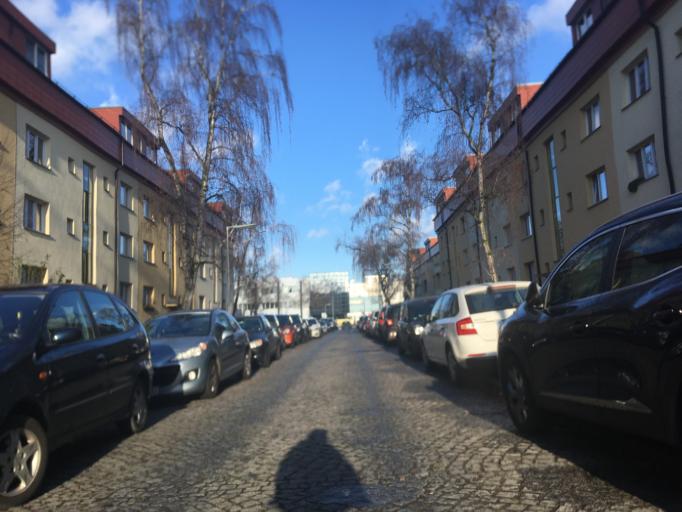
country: DE
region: Berlin
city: Reinickendorf
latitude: 52.5746
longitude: 13.3232
